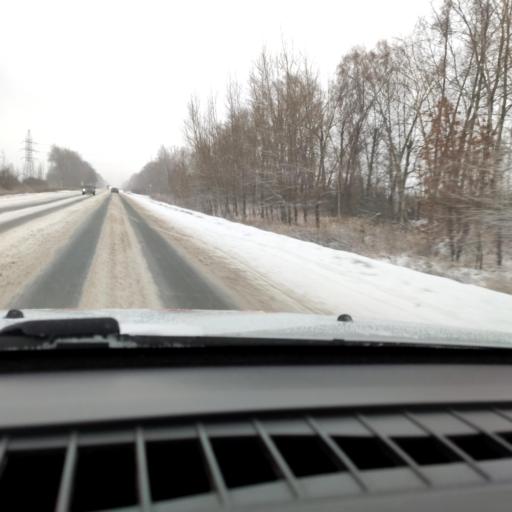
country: RU
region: Samara
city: Tol'yatti
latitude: 53.6184
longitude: 49.3111
